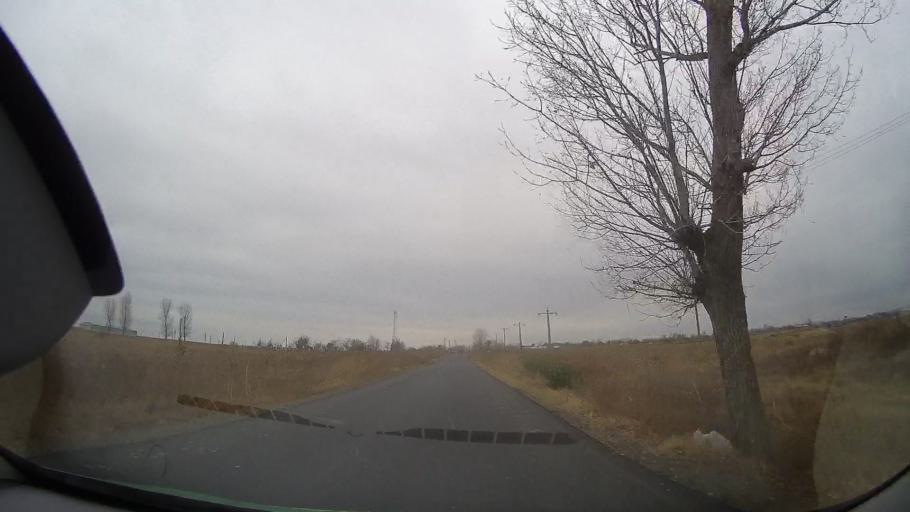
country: RO
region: Braila
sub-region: Comuna Ciresu
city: Ciresu
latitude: 44.9431
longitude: 27.3379
